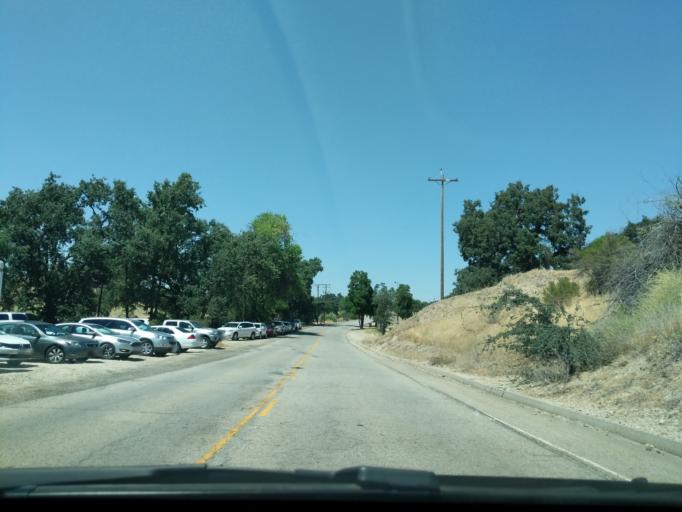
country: US
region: California
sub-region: San Luis Obispo County
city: Paso Robles
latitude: 35.6486
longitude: -120.6411
